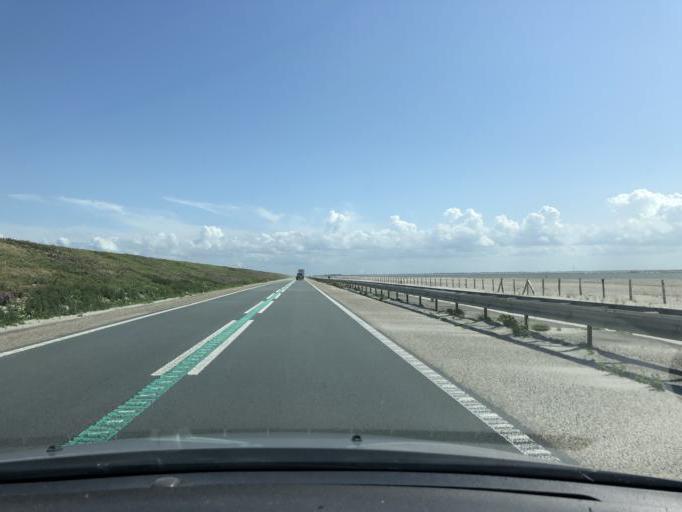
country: NL
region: North Holland
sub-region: Gemeente Enkhuizen
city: Enkhuizen
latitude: 52.6685
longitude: 5.3694
